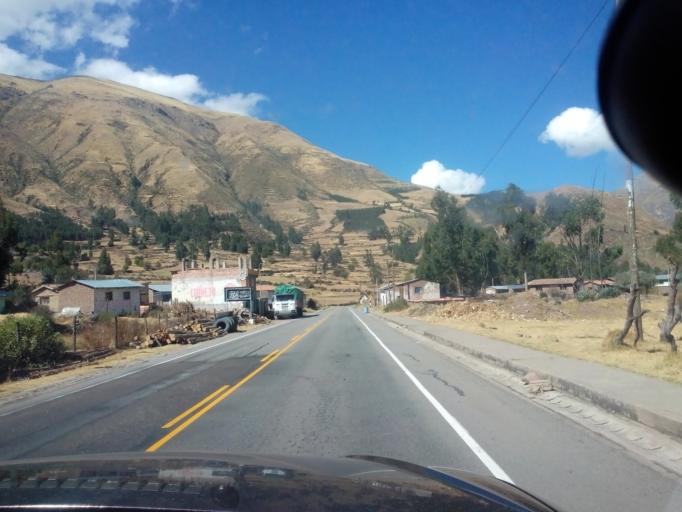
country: PE
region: Cusco
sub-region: Provincia de Quispicanchis
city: Cusipata
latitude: -13.9067
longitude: -71.4990
